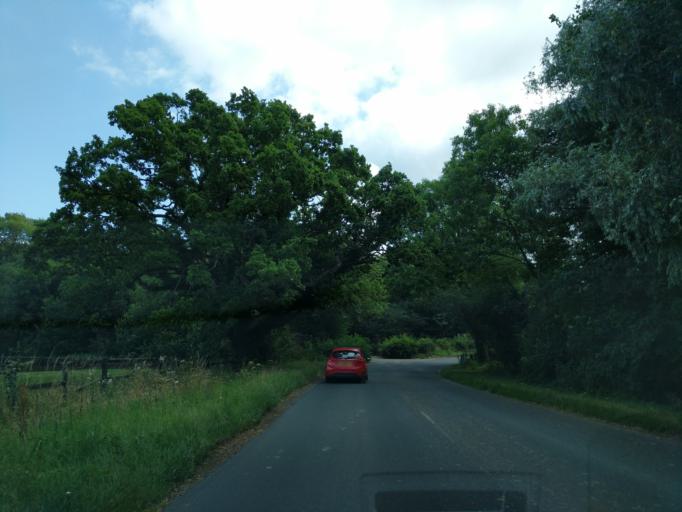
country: GB
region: England
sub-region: Cambridgeshire
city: Isleham
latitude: 52.2932
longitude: 0.4509
